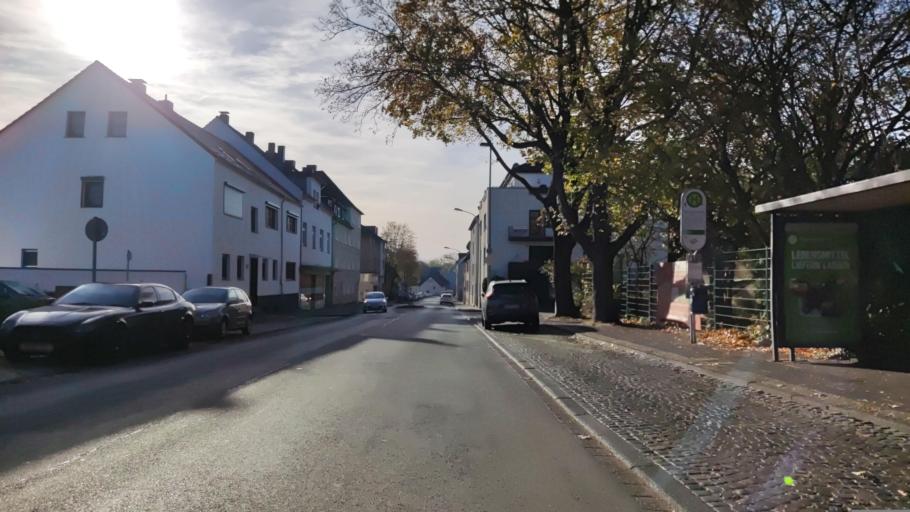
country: DE
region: North Rhine-Westphalia
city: Bochum-Hordel
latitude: 51.5262
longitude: 7.1839
